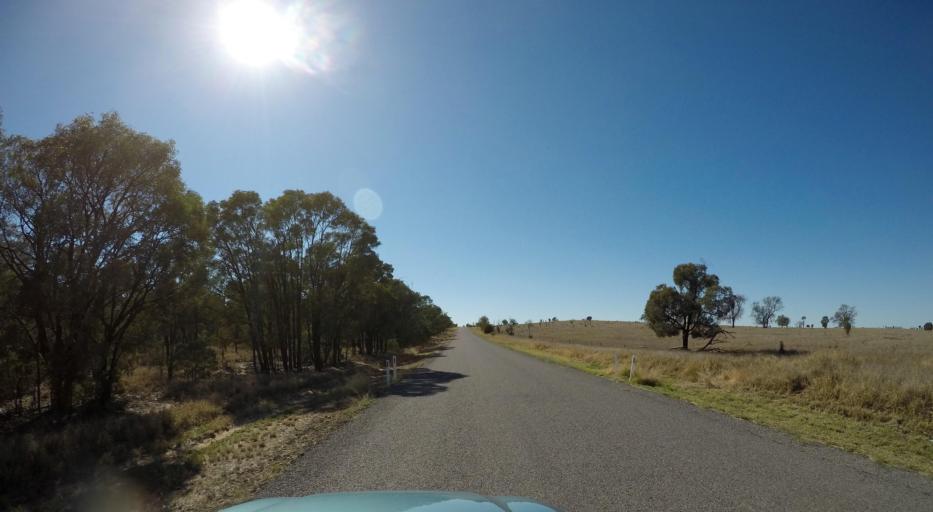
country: AU
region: Queensland
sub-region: Banana
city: Taroom
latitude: -25.7886
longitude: 149.6820
